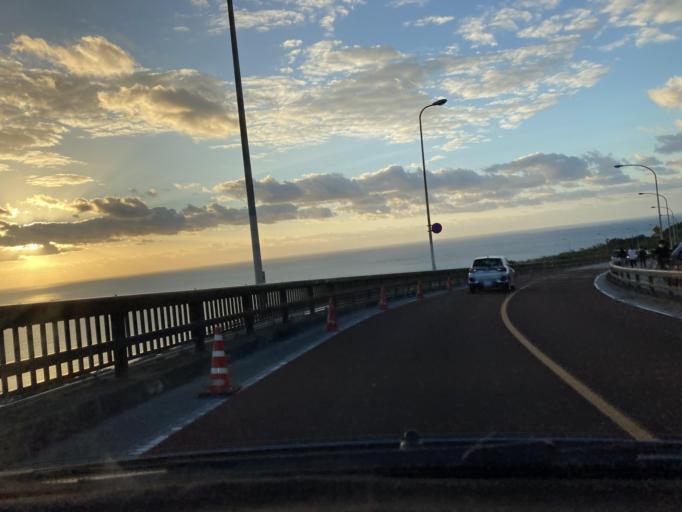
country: JP
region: Okinawa
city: Ginowan
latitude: 26.1669
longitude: 127.8158
